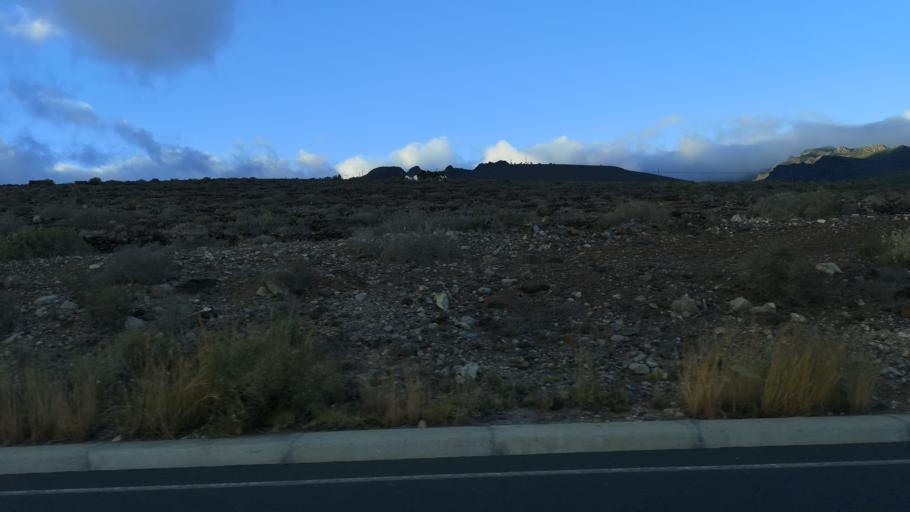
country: ES
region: Canary Islands
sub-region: Provincia de Santa Cruz de Tenerife
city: Alajero
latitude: 28.0331
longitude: -17.2167
